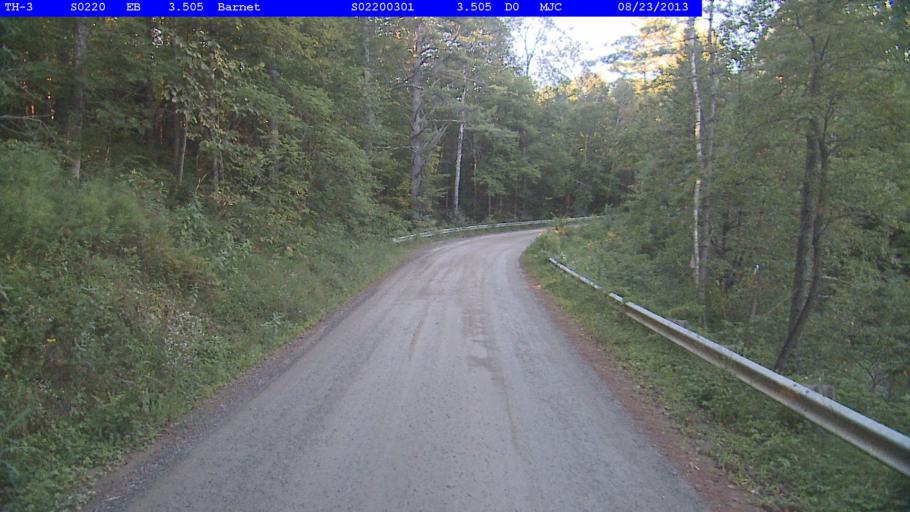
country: US
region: Vermont
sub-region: Caledonia County
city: Saint Johnsbury
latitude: 44.3437
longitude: -71.9933
